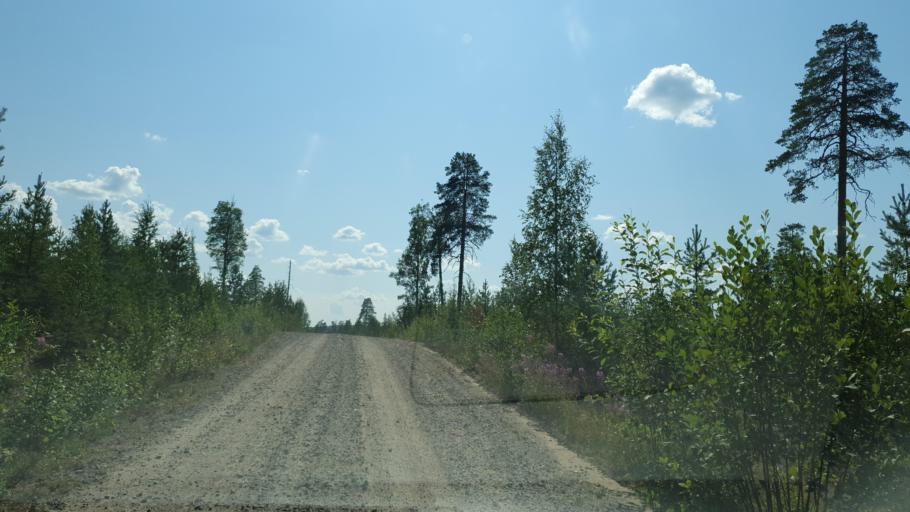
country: FI
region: Kainuu
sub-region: Kehys-Kainuu
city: Kuhmo
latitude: 63.9968
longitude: 29.5519
